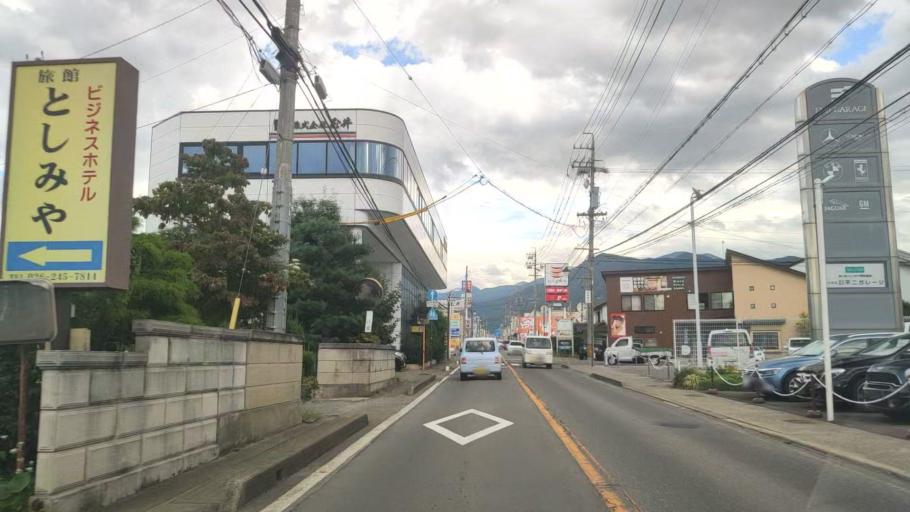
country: JP
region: Nagano
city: Suzaka
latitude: 36.6546
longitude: 138.2994
